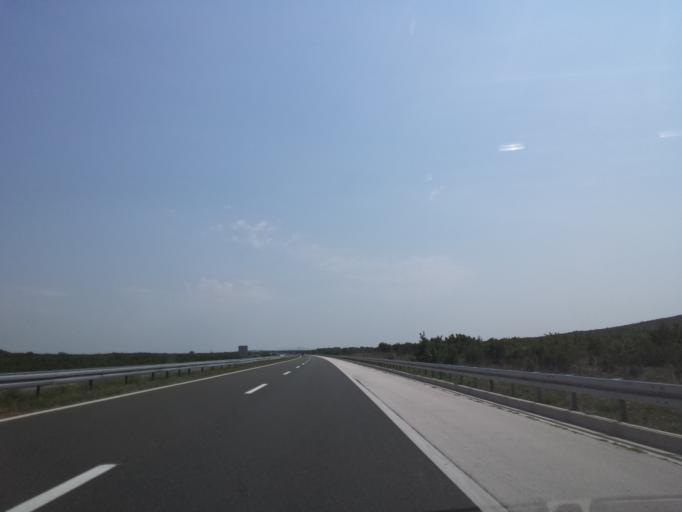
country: HR
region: Sibensko-Kniniska
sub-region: Grad Sibenik
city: Pirovac
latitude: 43.9379
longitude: 15.7045
